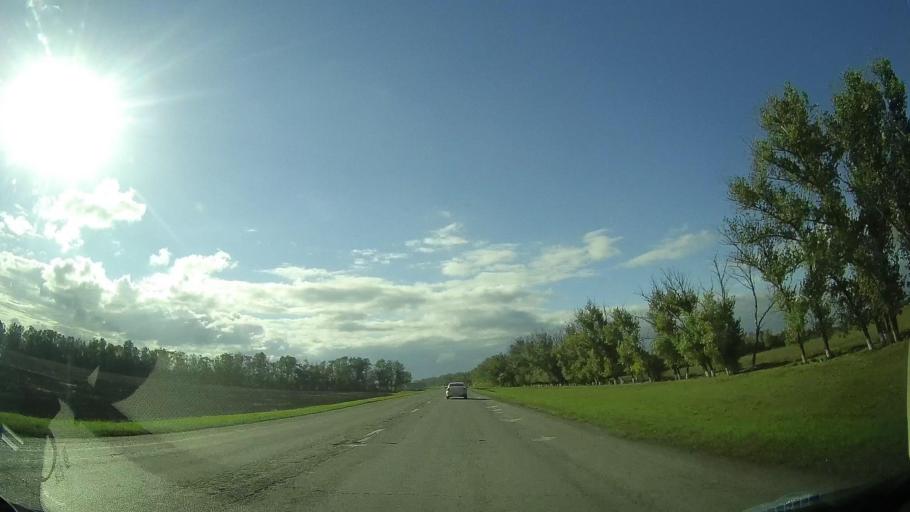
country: RU
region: Rostov
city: Tselina
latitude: 46.5328
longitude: 40.9936
